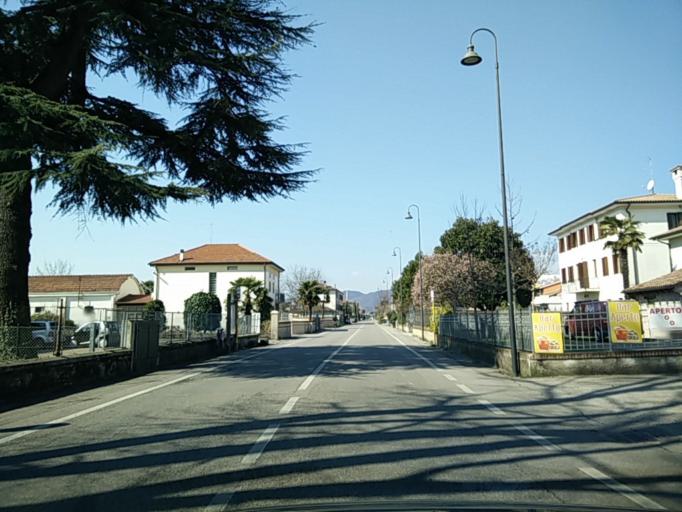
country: IT
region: Veneto
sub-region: Provincia di Treviso
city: Ciano
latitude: 45.8253
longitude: 12.0555
